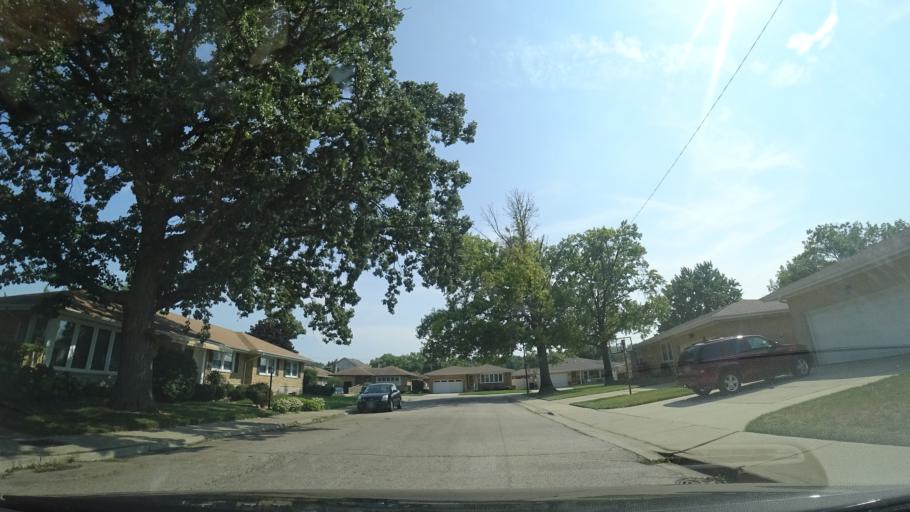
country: US
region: Illinois
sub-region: Cook County
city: Norridge
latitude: 41.9617
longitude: -87.8417
